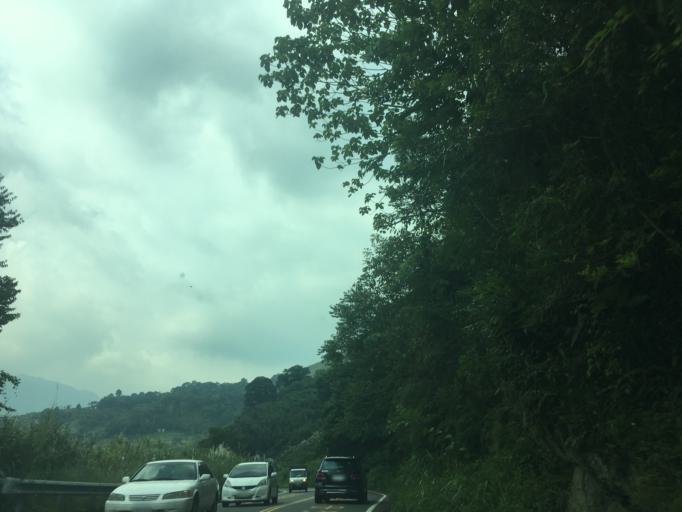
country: TW
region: Taiwan
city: Fengyuan
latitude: 24.3138
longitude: 120.9223
